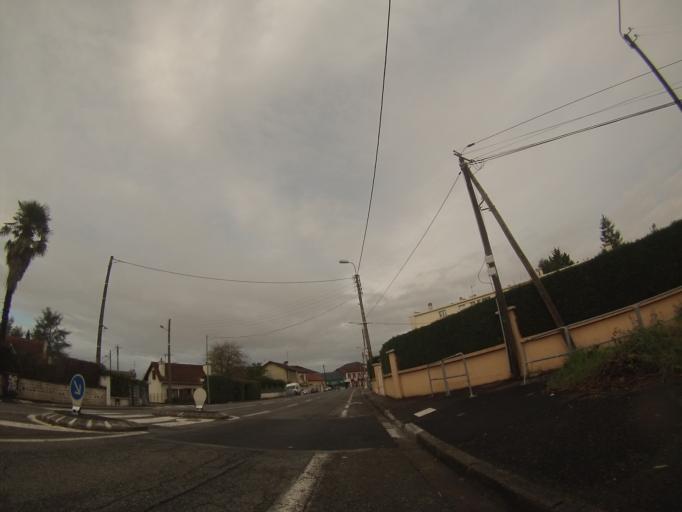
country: FR
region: Aquitaine
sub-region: Departement des Pyrenees-Atlantiques
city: Jurancon
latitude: 43.2819
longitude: -0.3873
